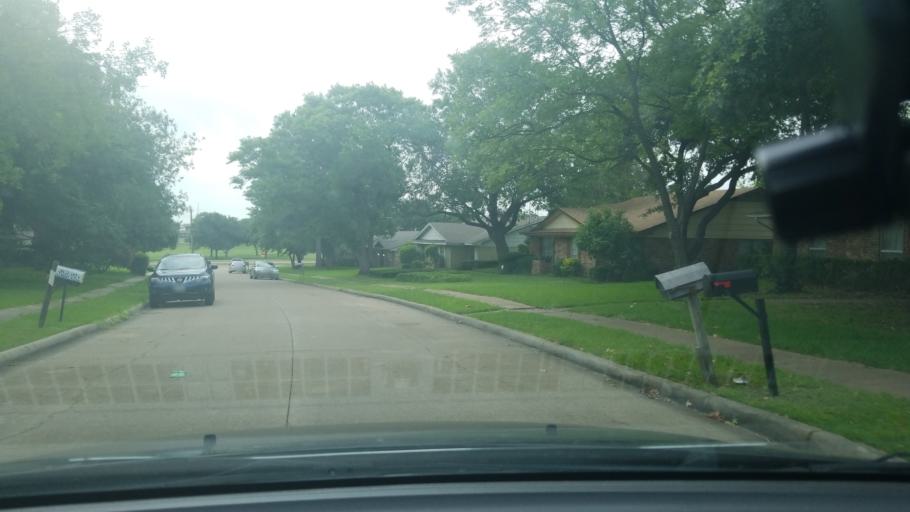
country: US
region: Texas
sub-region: Dallas County
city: Mesquite
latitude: 32.7850
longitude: -96.6414
